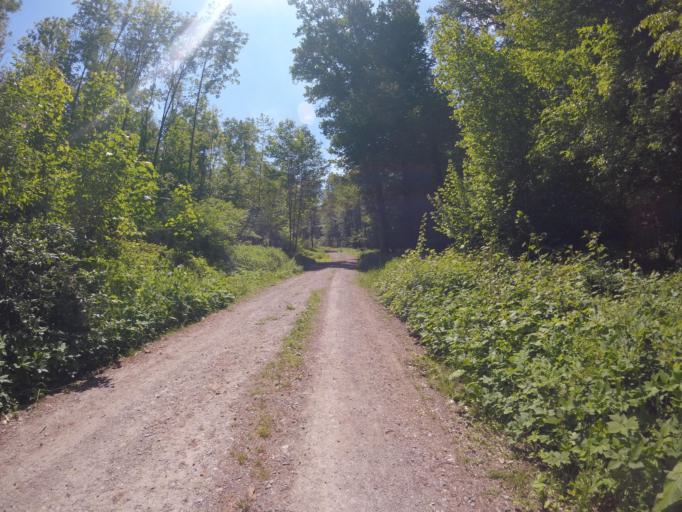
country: DE
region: Baden-Wuerttemberg
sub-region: Regierungsbezirk Stuttgart
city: Mittelschontal
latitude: 48.9281
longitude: 9.4091
